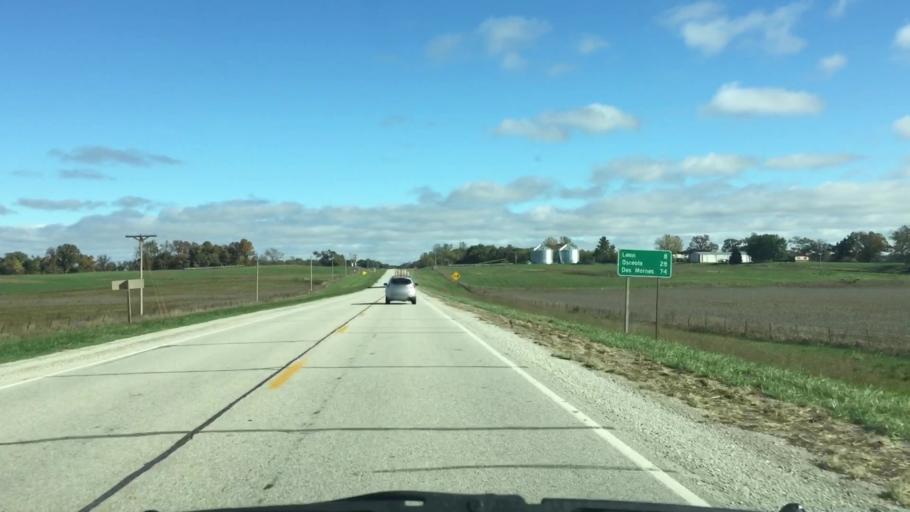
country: US
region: Iowa
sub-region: Decatur County
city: Leon
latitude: 40.6443
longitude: -93.8055
